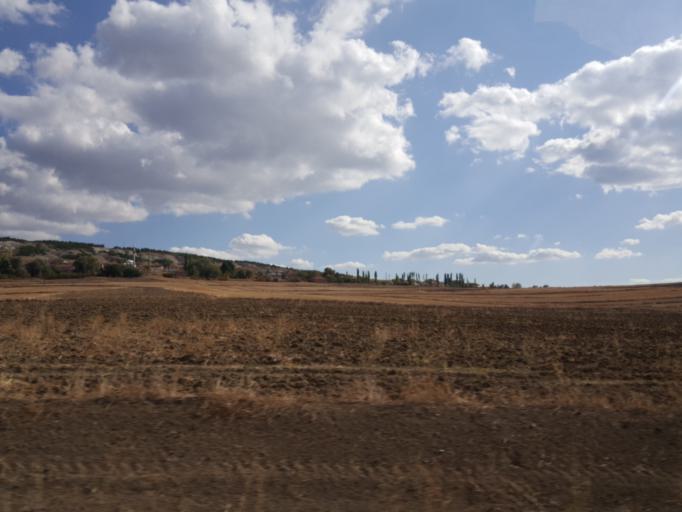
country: TR
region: Tokat
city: Sulusaray
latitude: 39.9882
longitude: 35.9872
